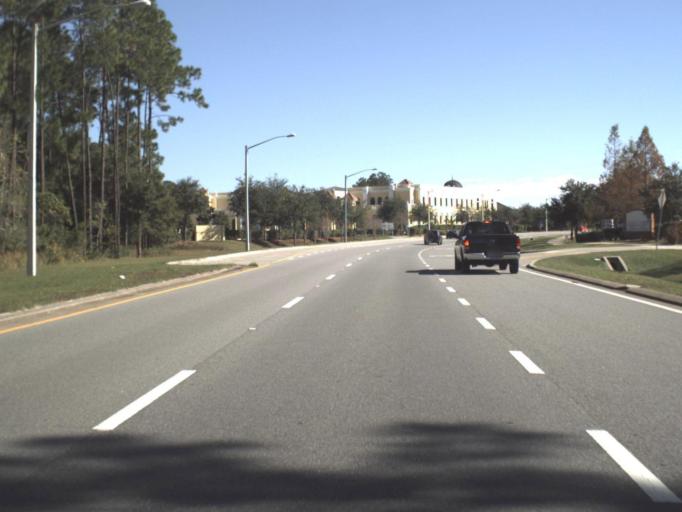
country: US
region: Florida
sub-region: Flagler County
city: Palm Coast
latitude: 29.5514
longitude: -81.2445
